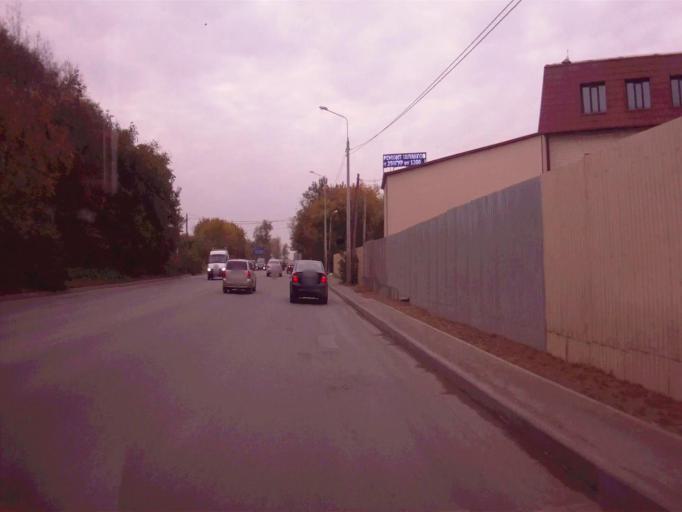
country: RU
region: Chelyabinsk
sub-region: Gorod Chelyabinsk
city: Chelyabinsk
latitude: 55.1292
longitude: 61.3854
